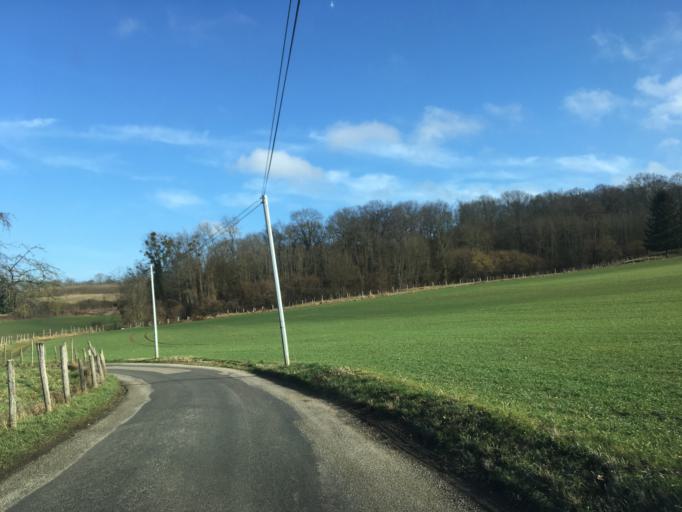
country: FR
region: Haute-Normandie
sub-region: Departement de l'Eure
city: La Chapelle-Reanville
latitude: 49.1152
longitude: 1.3981
